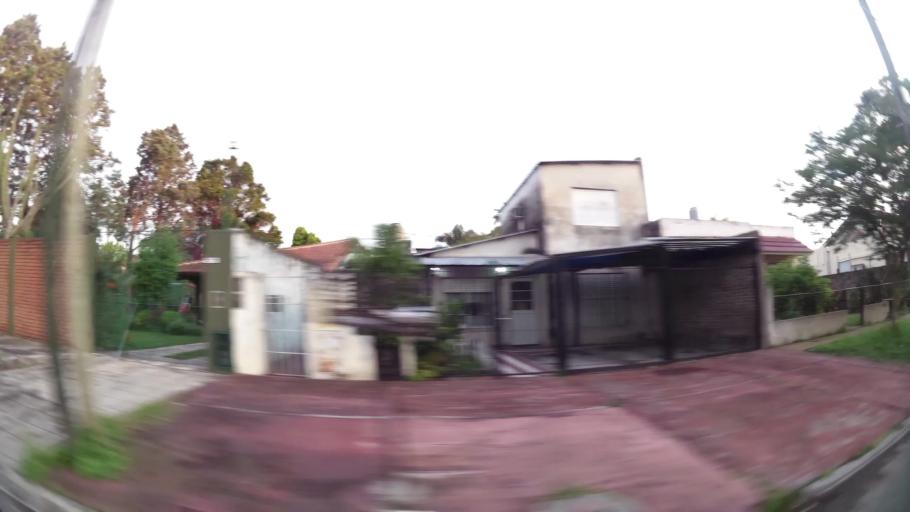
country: AR
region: Buenos Aires
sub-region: Partido de Lomas de Zamora
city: Lomas de Zamora
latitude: -34.7689
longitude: -58.3800
